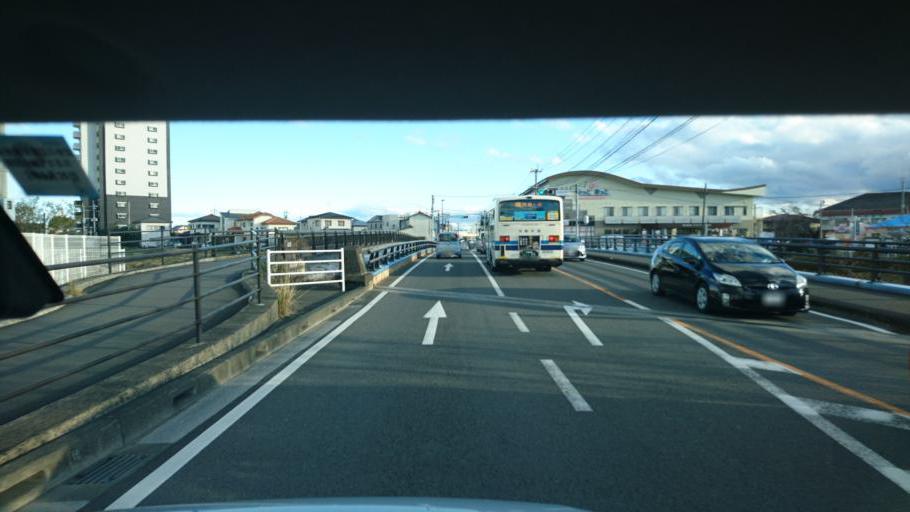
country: JP
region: Miyazaki
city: Miyazaki-shi
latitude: 31.8884
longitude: 131.4232
